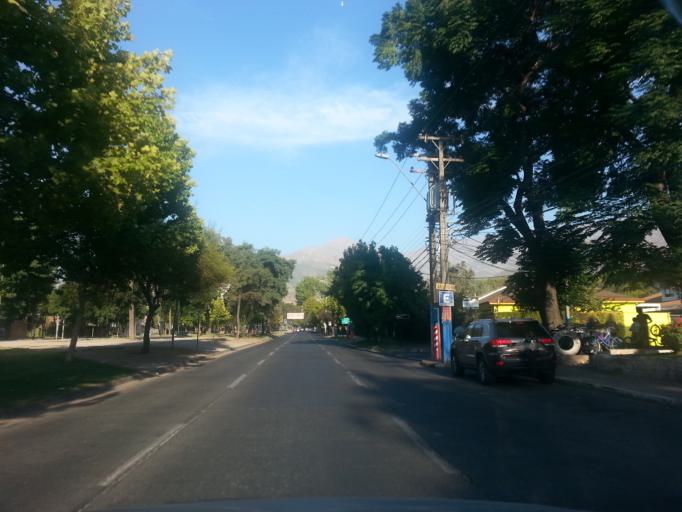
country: CL
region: Santiago Metropolitan
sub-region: Provincia de Santiago
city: Villa Presidente Frei, Nunoa, Santiago, Chile
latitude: -33.4306
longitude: -70.5535
